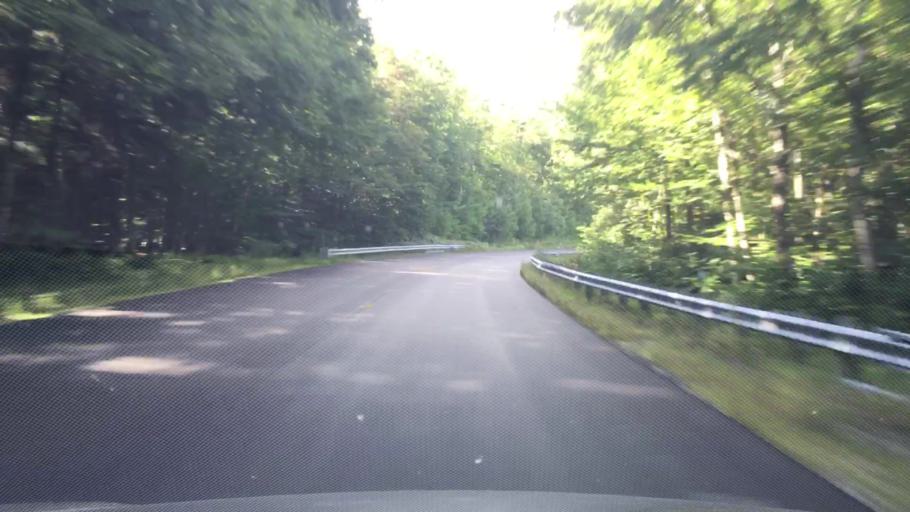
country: US
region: New Hampshire
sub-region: Carroll County
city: Sandwich
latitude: 44.0087
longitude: -71.4269
